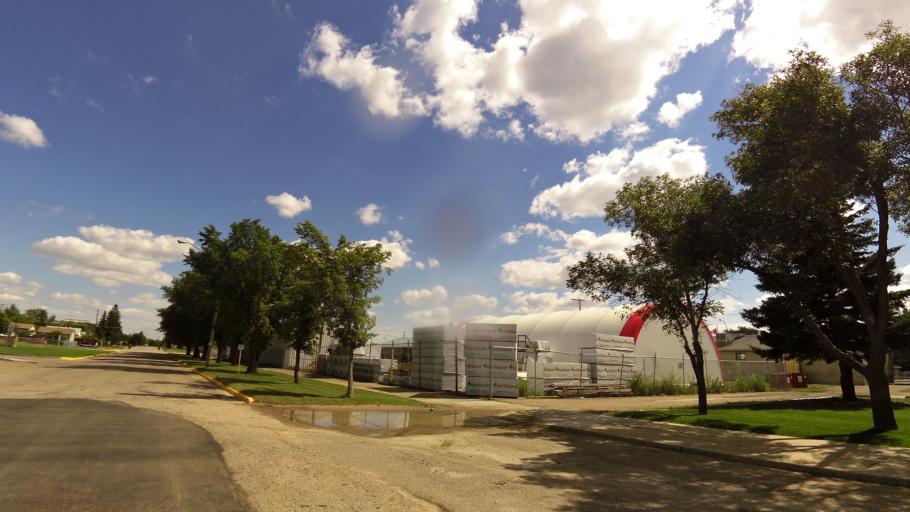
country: CA
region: Saskatchewan
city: North Battleford
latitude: 52.7371
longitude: -108.3109
